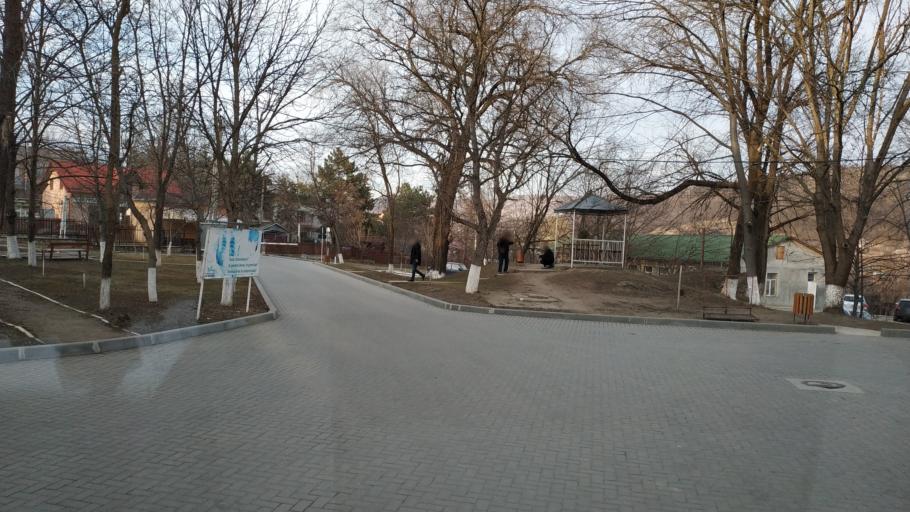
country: MD
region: Nisporeni
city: Nisporeni
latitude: 47.0876
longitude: 28.1770
